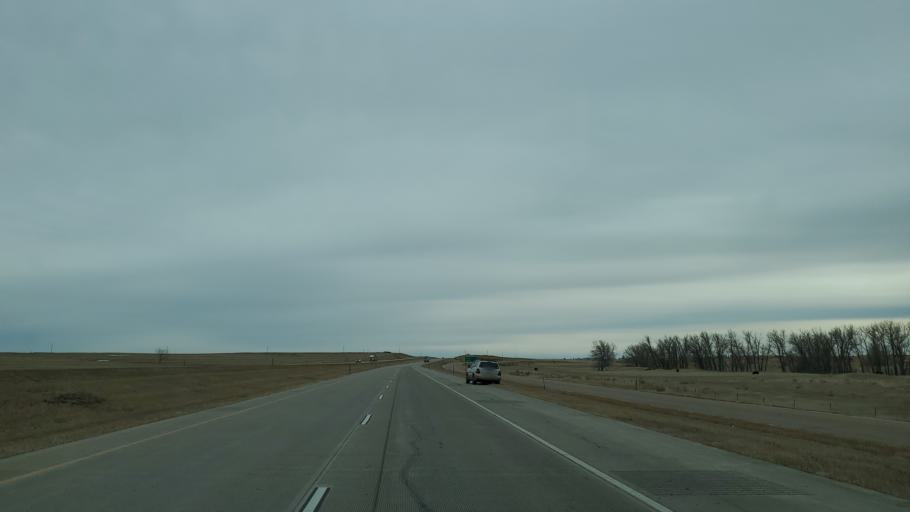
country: US
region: Colorado
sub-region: Arapahoe County
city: Byers
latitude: 39.4937
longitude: -103.9620
